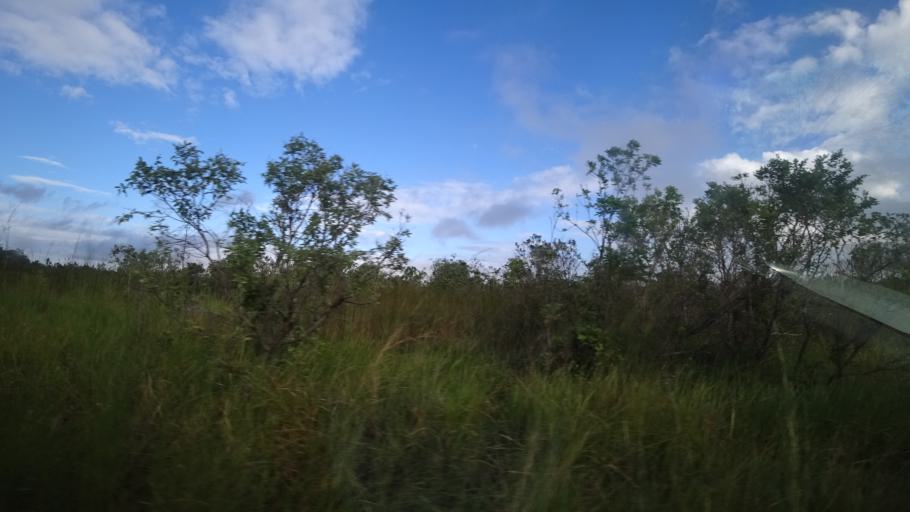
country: MZ
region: Sofala
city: Beira
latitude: -19.6498
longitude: 35.0583
